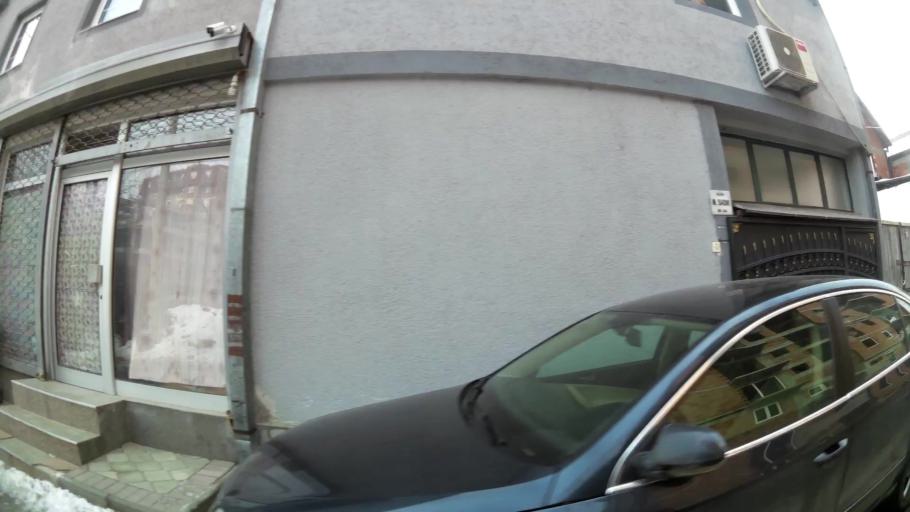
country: MK
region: Cair
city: Cair
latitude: 42.0122
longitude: 21.4356
